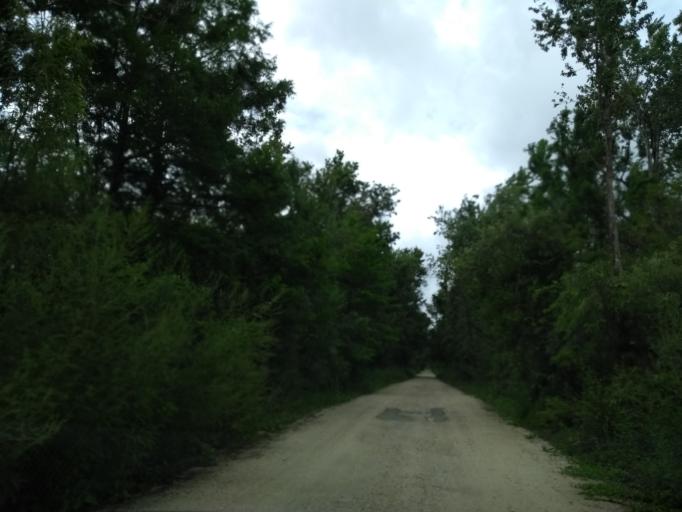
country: US
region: Florida
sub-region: Collier County
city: Lely Resort
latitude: 25.9857
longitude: -81.4110
